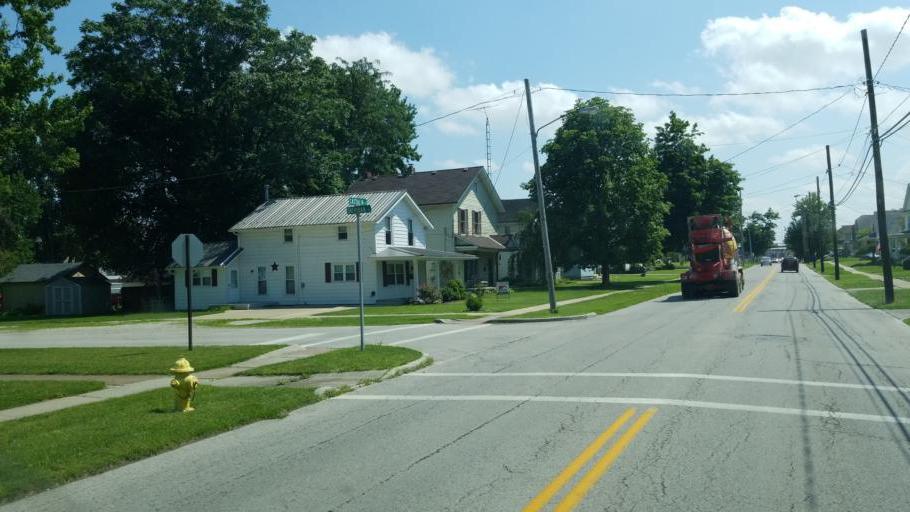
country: US
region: Ohio
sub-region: Huron County
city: Bellevue
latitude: 41.2790
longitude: -82.8395
